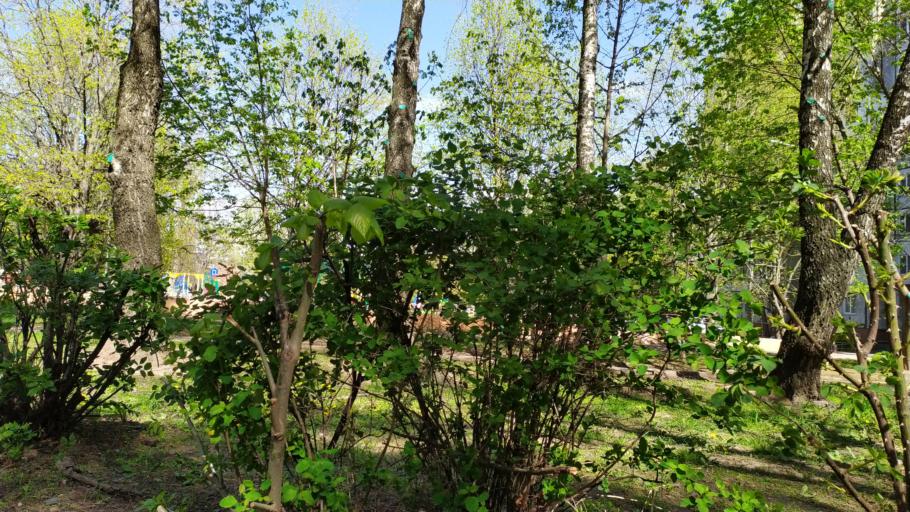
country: RU
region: Kursk
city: Kursk
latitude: 51.7393
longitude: 36.1368
